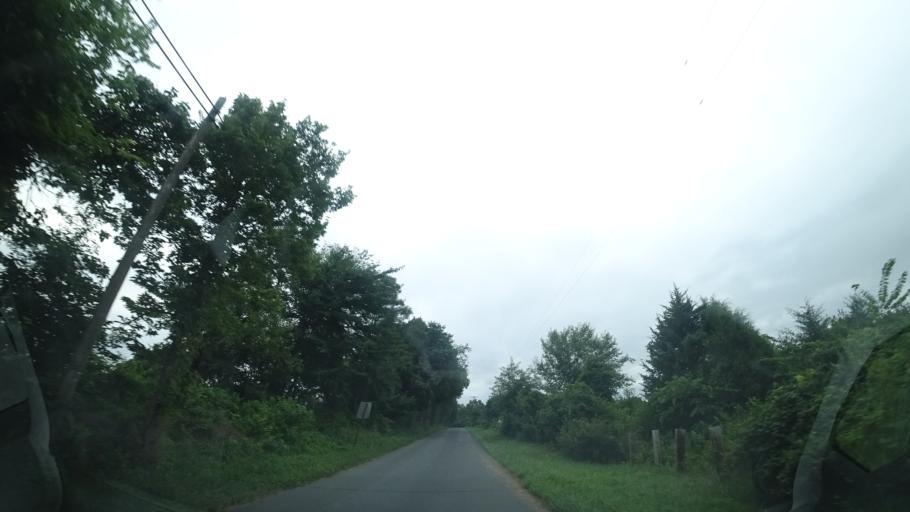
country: US
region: Maryland
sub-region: Montgomery County
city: Poolesville
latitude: 39.1135
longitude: -77.4362
